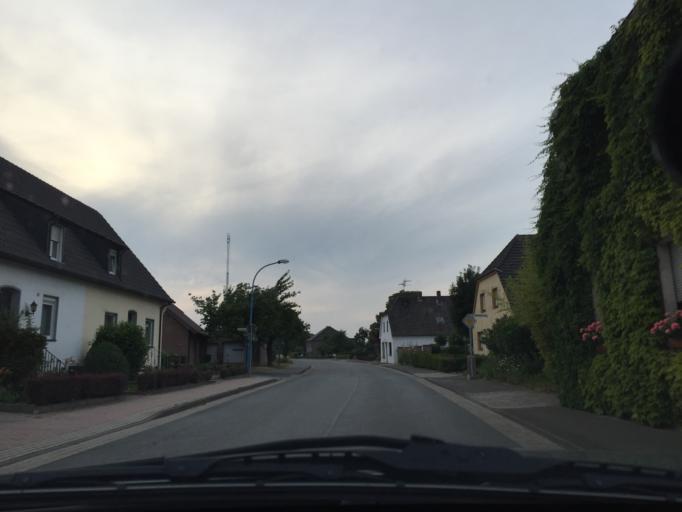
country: DE
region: North Rhine-Westphalia
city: Kalkar
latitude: 51.7639
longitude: 6.2571
